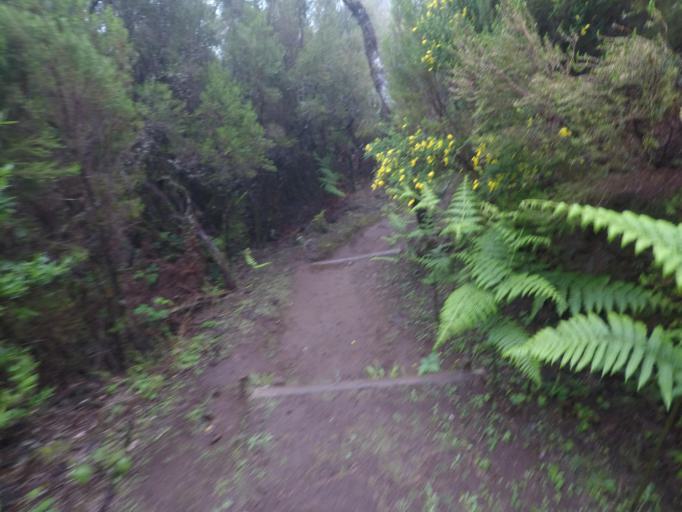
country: PT
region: Madeira
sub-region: Calheta
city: Arco da Calheta
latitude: 32.7681
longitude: -17.1131
